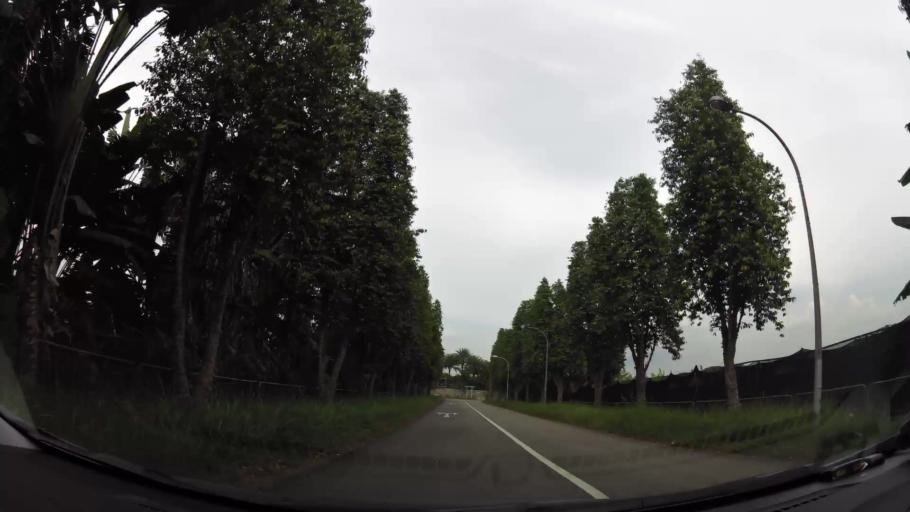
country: MY
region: Johor
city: Johor Bahru
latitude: 1.4429
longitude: 103.7119
